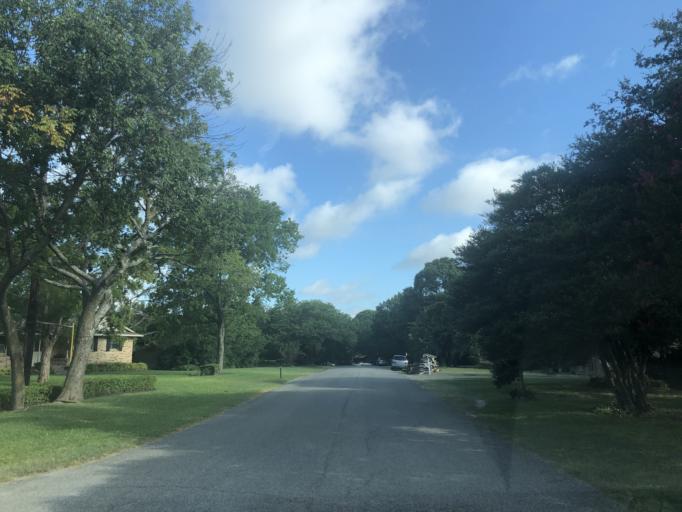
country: US
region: Texas
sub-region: Dallas County
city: Duncanville
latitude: 32.6650
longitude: -96.9191
